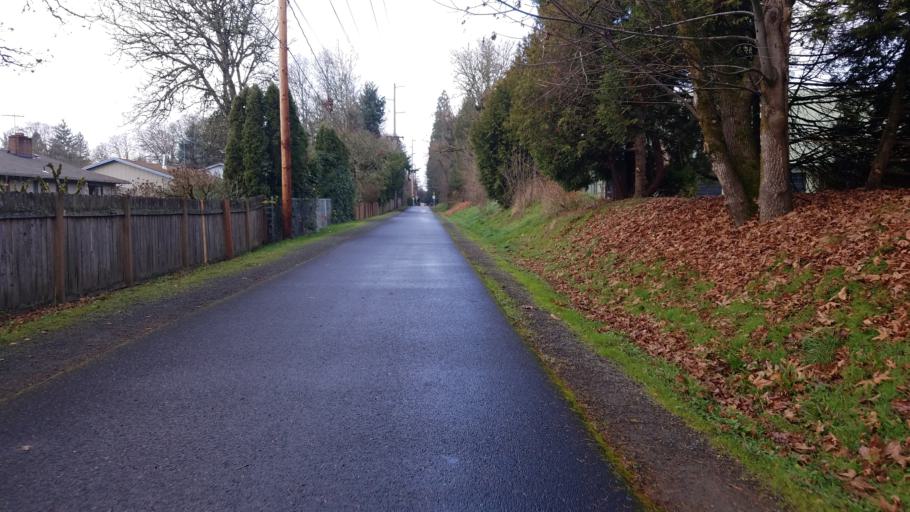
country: US
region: Oregon
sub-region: Clackamas County
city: Jennings Lodge
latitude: 45.4014
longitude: -122.6279
